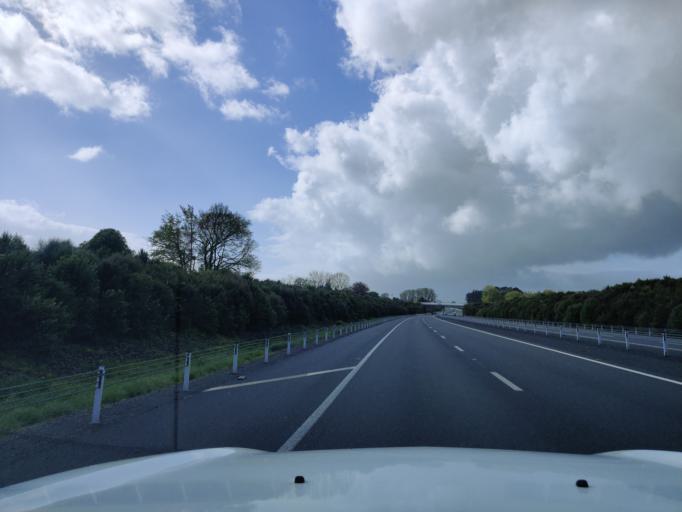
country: NZ
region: Waikato
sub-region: Waipa District
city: Cambridge
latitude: -37.8817
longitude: 175.4898
